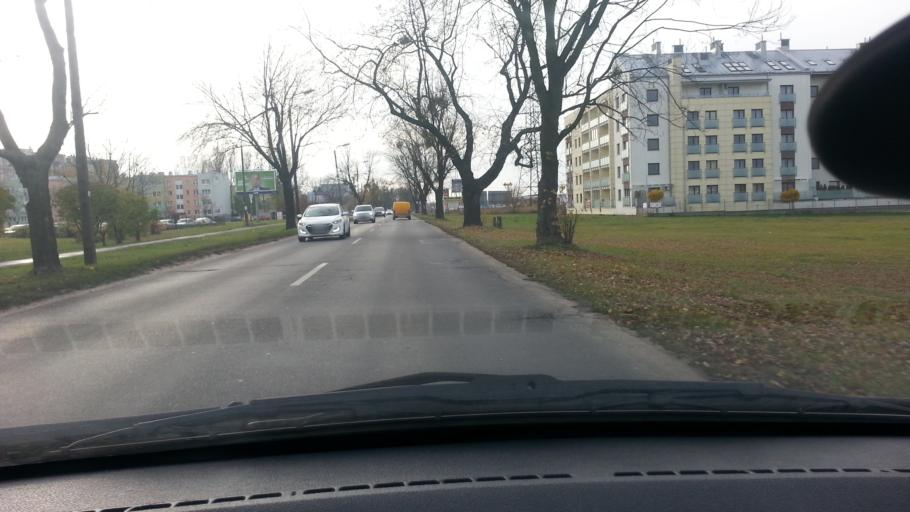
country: PL
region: Masovian Voivodeship
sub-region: Warszawa
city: Bemowo
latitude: 52.2334
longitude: 20.8967
